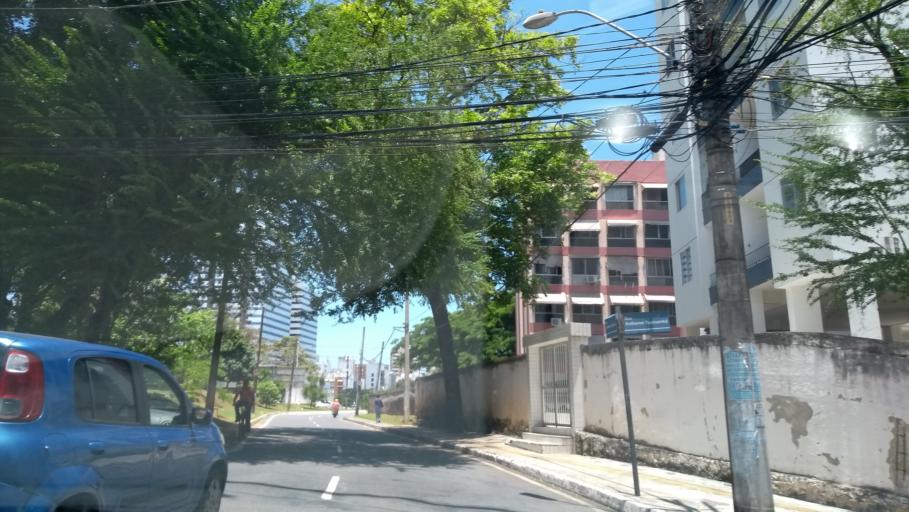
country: BR
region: Bahia
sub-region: Salvador
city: Salvador
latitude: -12.9908
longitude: -38.4513
